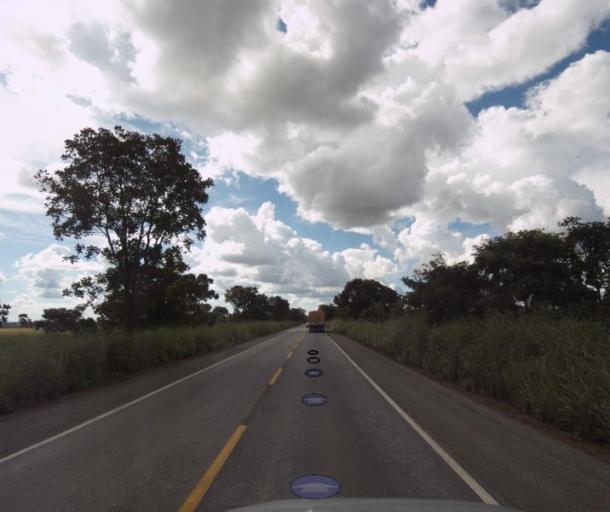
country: BR
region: Goias
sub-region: Porangatu
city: Porangatu
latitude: -13.2812
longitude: -49.1280
